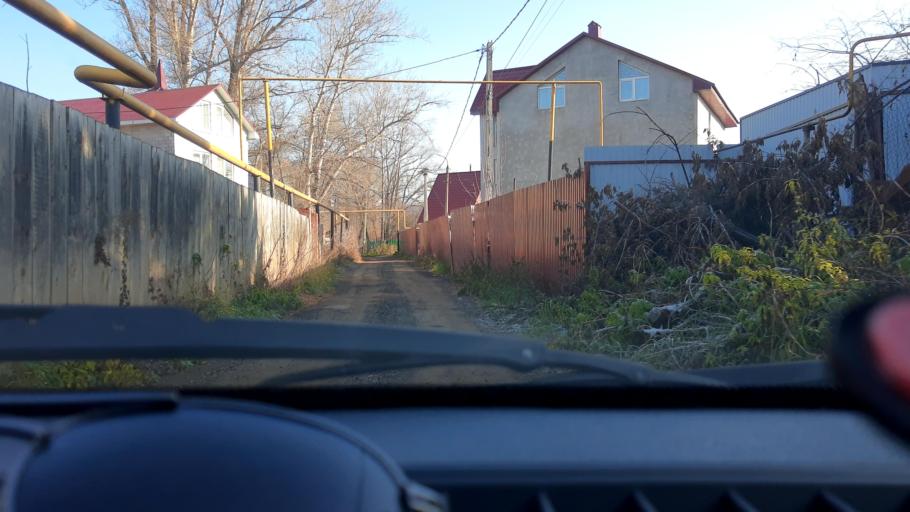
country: RU
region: Bashkortostan
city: Ufa
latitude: 54.6956
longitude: 55.9421
